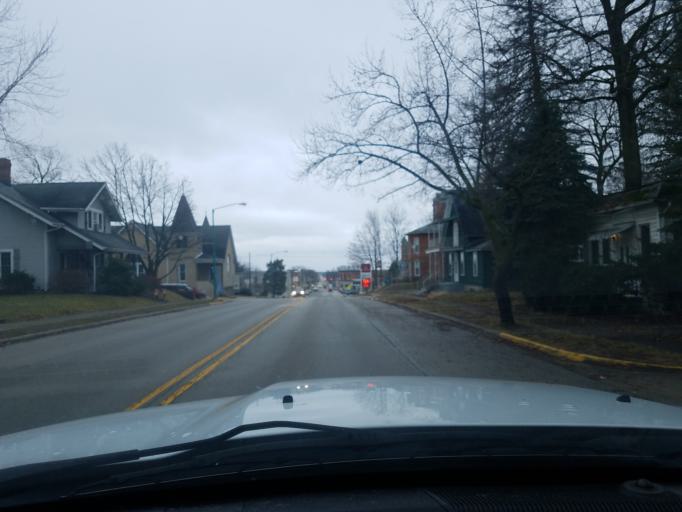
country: US
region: Indiana
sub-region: Noble County
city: Albion
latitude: 41.3980
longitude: -85.4240
